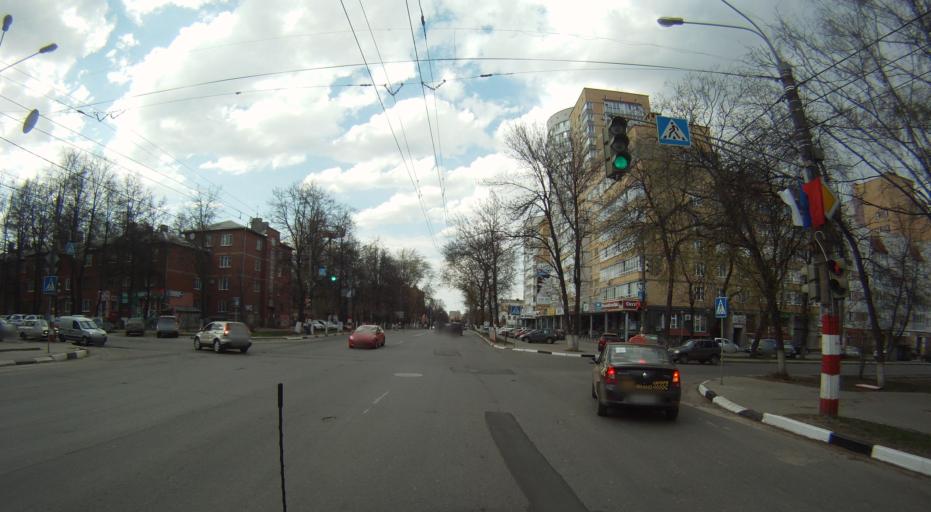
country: RU
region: Nizjnij Novgorod
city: Nizhniy Novgorod
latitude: 56.3130
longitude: 44.0190
